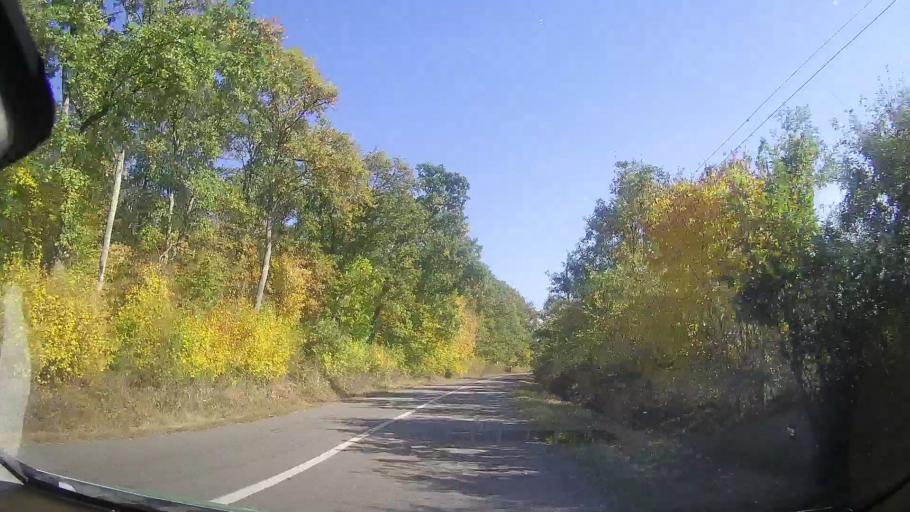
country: RO
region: Timis
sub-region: Comuna Ghizela
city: Ghizela
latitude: 45.8375
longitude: 21.7766
